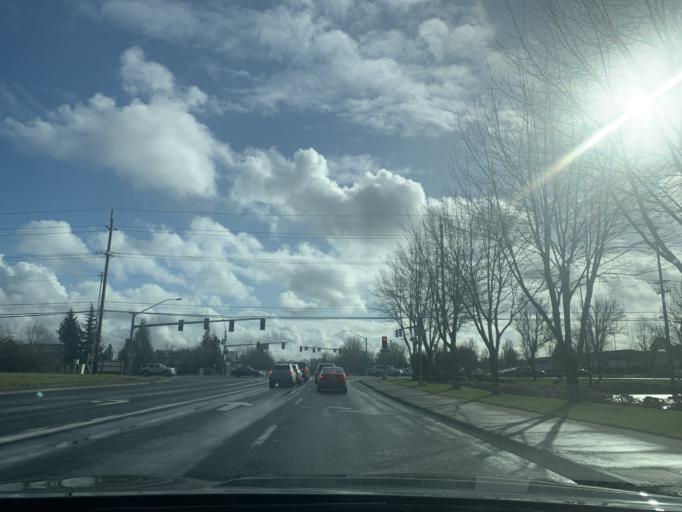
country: US
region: Oregon
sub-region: Washington County
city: Sherwood
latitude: 45.3706
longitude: -122.8441
